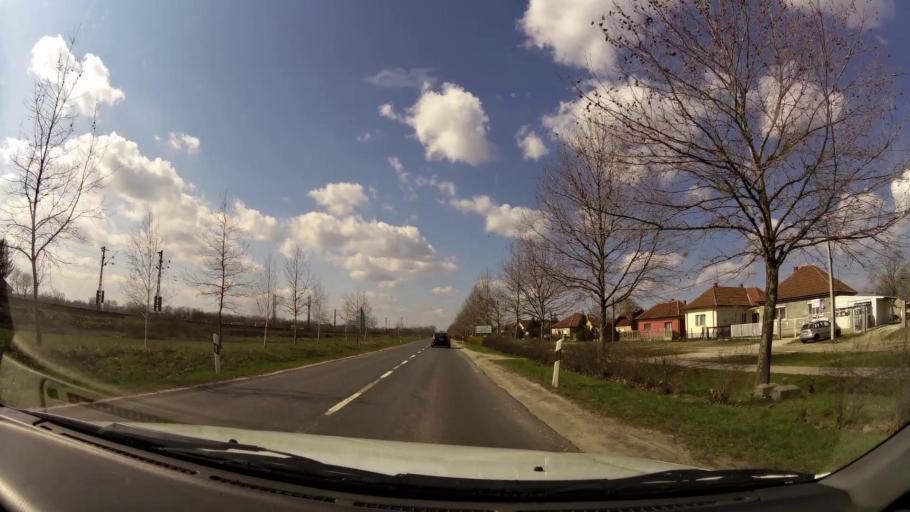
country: HU
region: Pest
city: Nagykata
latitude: 47.3985
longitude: 19.7581
